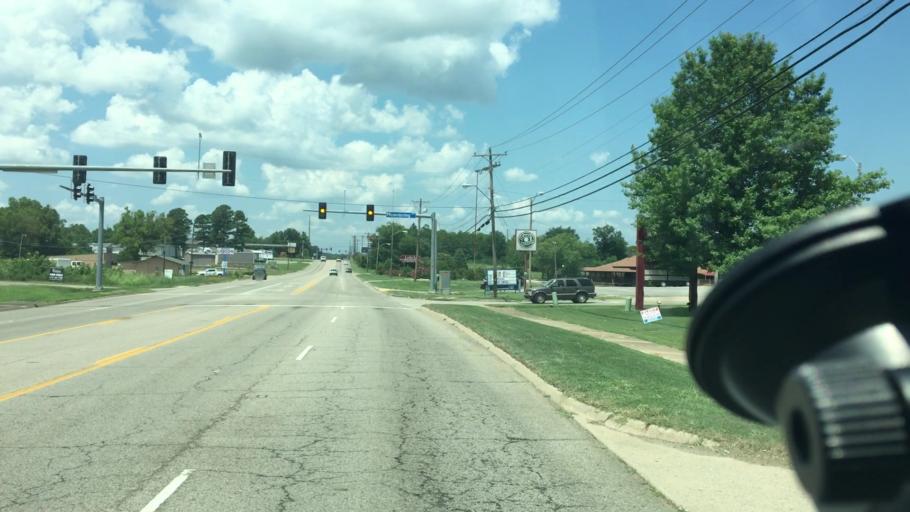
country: US
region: Arkansas
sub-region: Sebastian County
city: Barling
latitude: 35.3437
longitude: -94.3264
